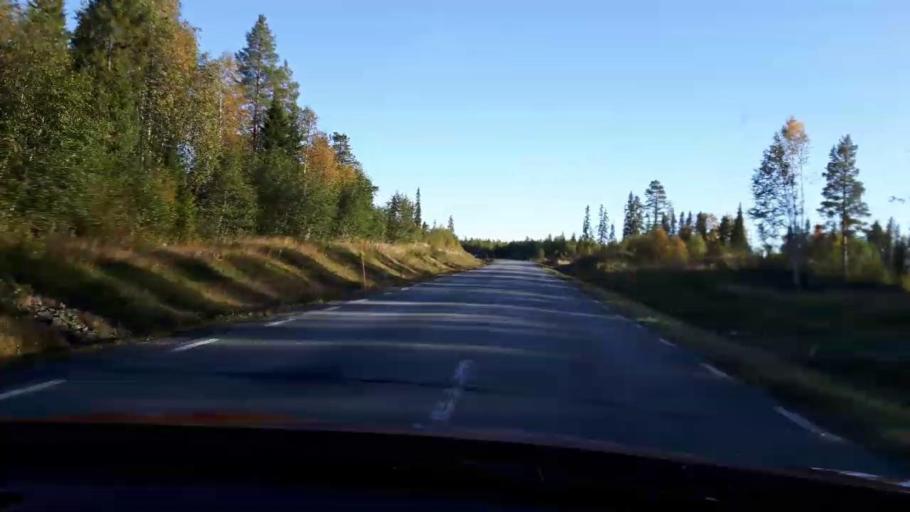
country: SE
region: Jaemtland
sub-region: OEstersunds Kommun
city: Lit
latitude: 63.7823
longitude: 14.7061
